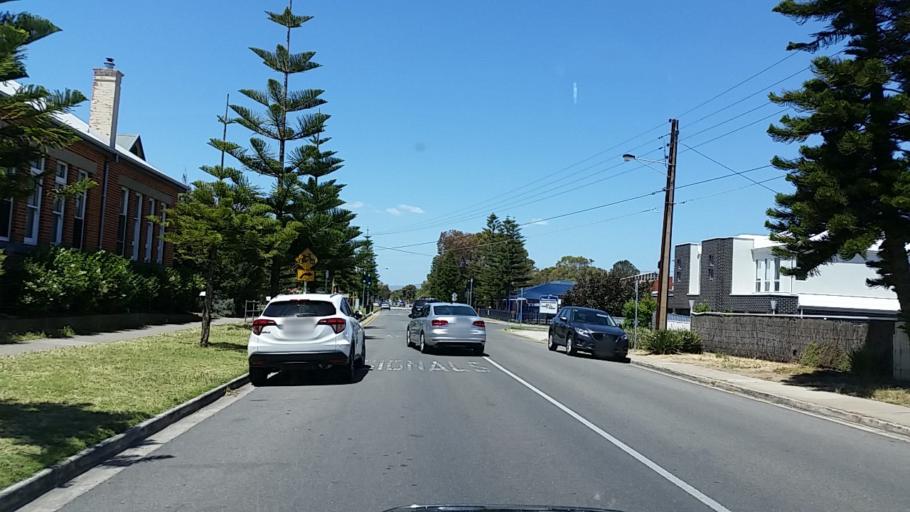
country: AU
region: South Australia
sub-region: Charles Sturt
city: Grange
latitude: -34.9022
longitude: 138.4955
